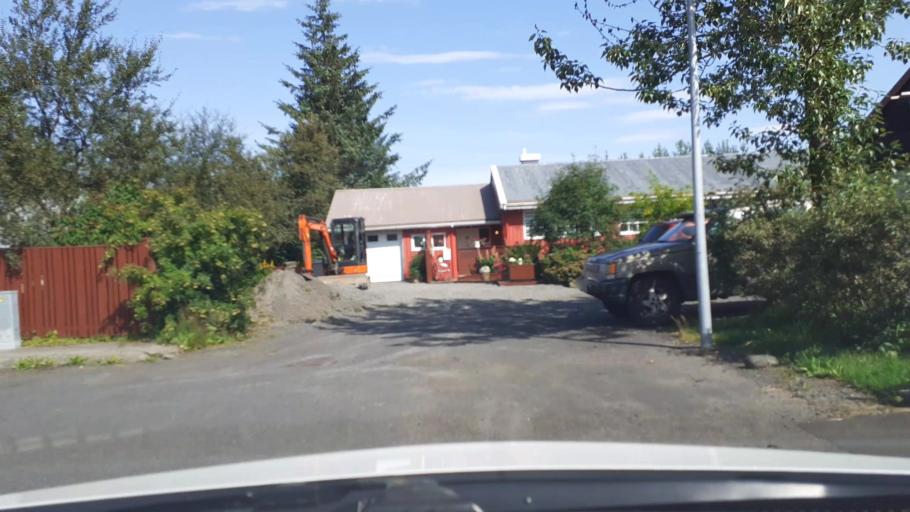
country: IS
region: South
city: Selfoss
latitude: 63.9285
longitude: -21.0074
